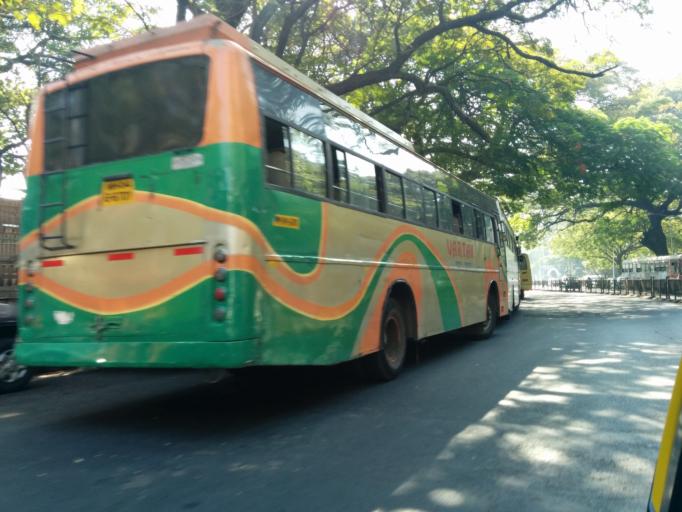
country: IN
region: Maharashtra
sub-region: Raigarh
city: Uran
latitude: 18.9268
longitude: 72.8314
